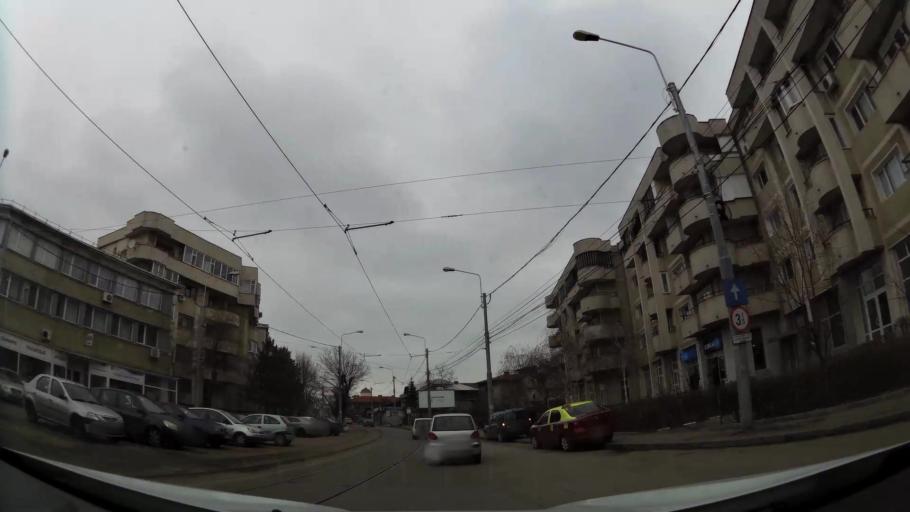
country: RO
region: Prahova
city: Ploiesti
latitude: 44.9344
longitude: 26.0316
